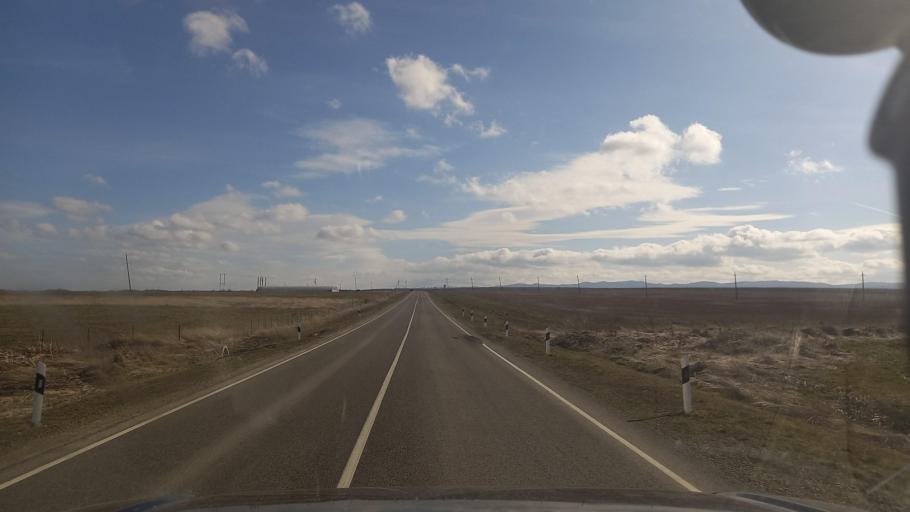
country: RU
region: Krasnodarskiy
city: Novodmitriyevskaya
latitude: 44.8068
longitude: 38.9079
